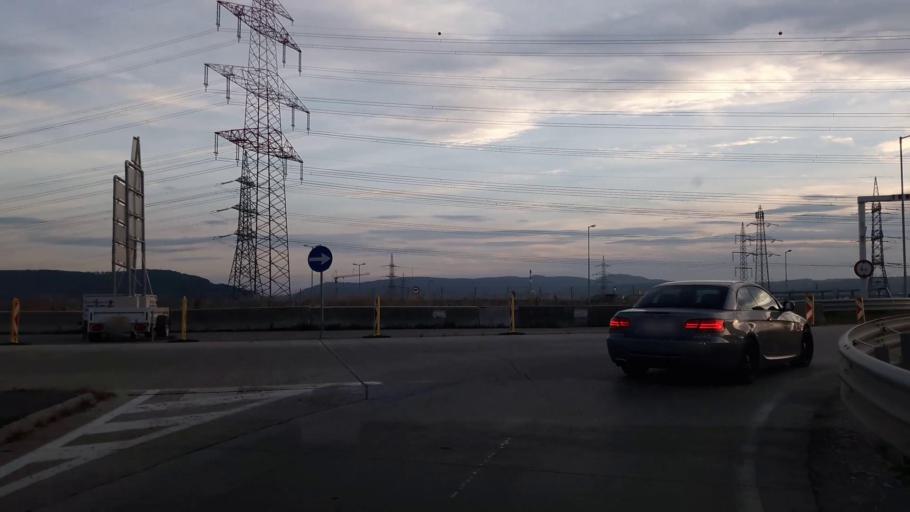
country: AT
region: Lower Austria
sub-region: Politischer Bezirk Korneuburg
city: Harmannsdorf
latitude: 48.3650
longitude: 16.3551
